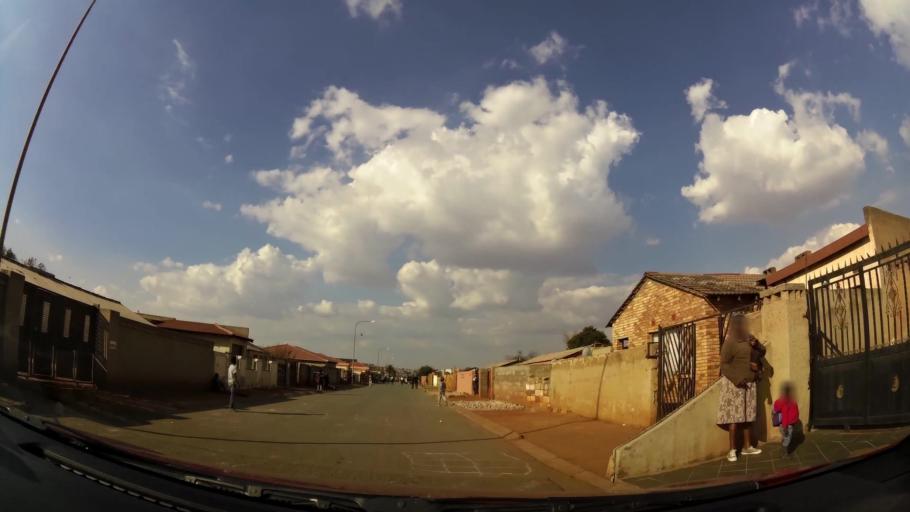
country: ZA
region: Gauteng
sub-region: City of Johannesburg Metropolitan Municipality
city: Soweto
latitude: -26.2241
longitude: 27.8651
